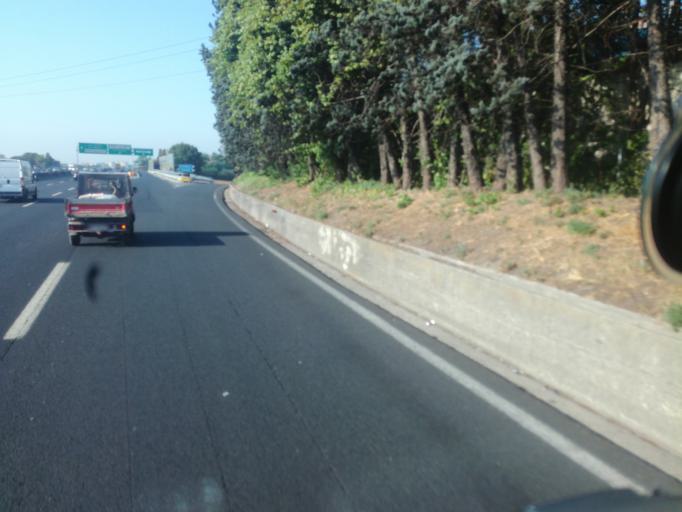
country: IT
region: Campania
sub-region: Provincia di Napoli
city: Arpino
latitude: 40.8993
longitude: 14.3189
